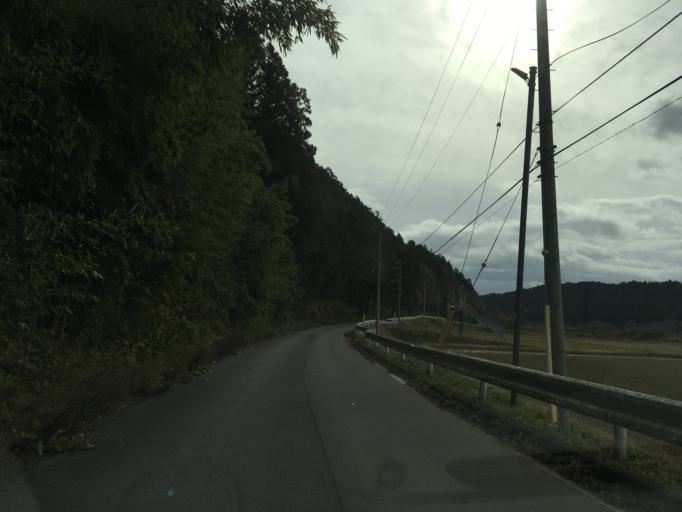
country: JP
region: Iwate
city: Ichinoseki
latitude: 38.7793
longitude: 141.2683
